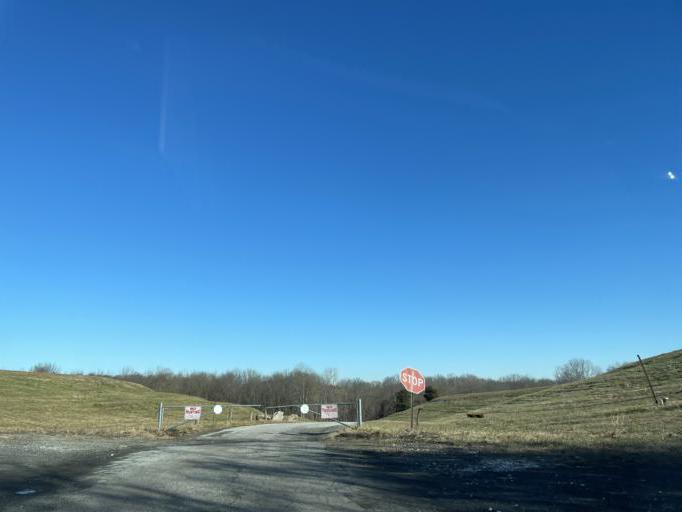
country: US
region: Pennsylvania
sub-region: York County
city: New Freedom
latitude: 39.6621
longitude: -76.6464
